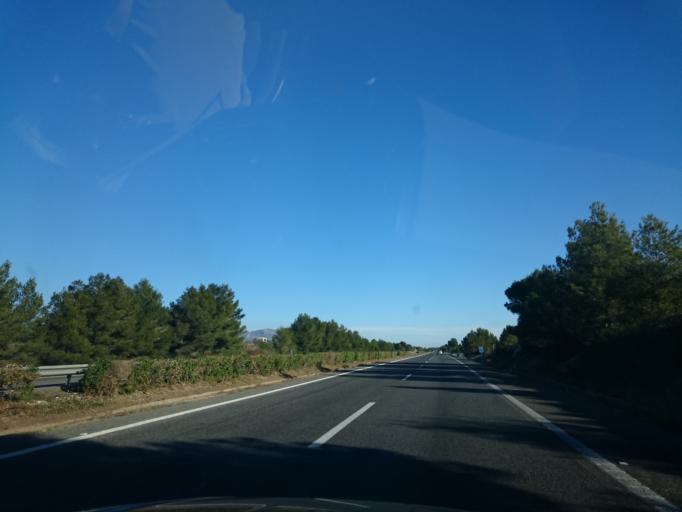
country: ES
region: Catalonia
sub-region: Provincia de Tarragona
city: l'Ametlla de Mar
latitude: 40.8654
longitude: 0.7759
